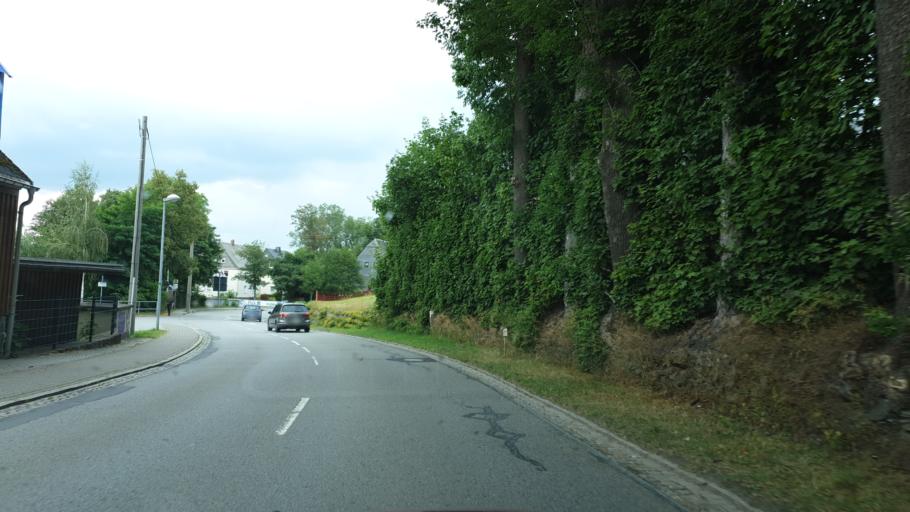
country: DE
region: Saxony
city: Zwonitz
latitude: 50.6408
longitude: 12.8193
